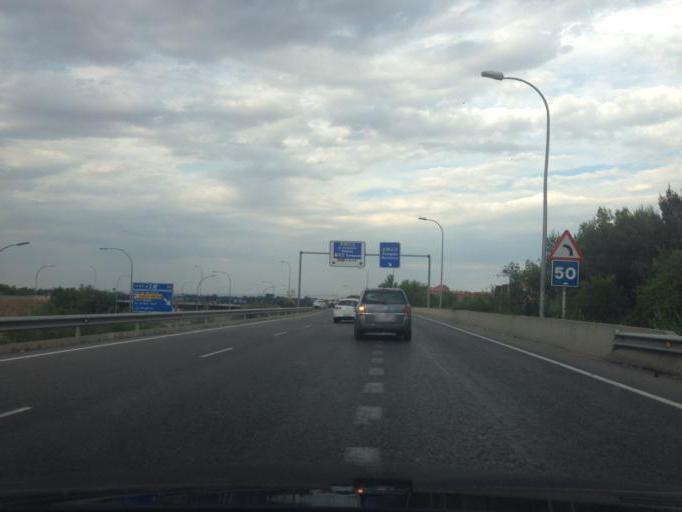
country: ES
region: Madrid
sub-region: Provincia de Madrid
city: Torrejon de Ardoz
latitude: 40.4641
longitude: -3.4838
